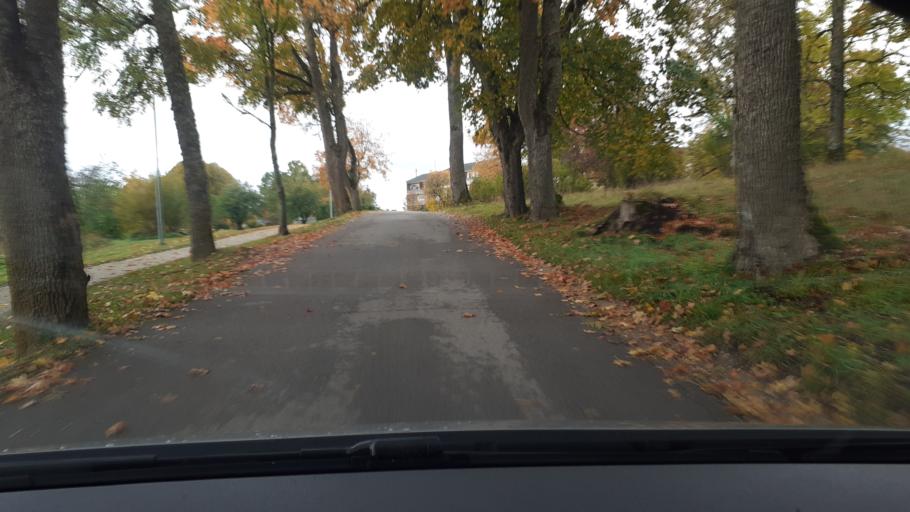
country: LV
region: Kuldigas Rajons
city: Kuldiga
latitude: 57.0181
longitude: 21.9095
